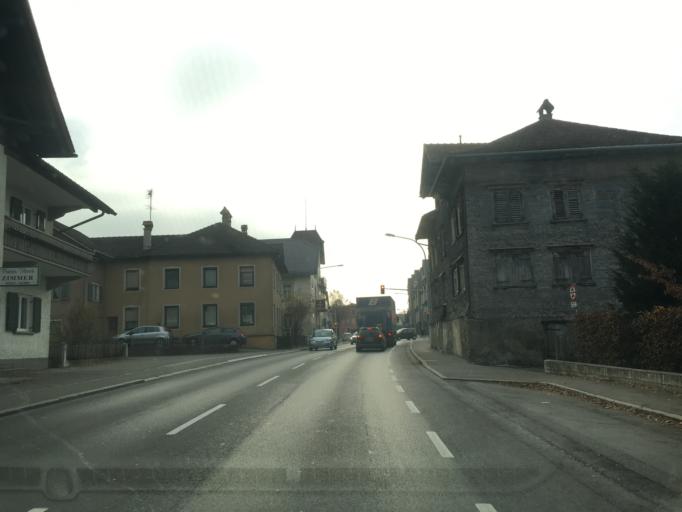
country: AT
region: Vorarlberg
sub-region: Politischer Bezirk Feldkirch
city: Altach
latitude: 47.3364
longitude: 9.6497
